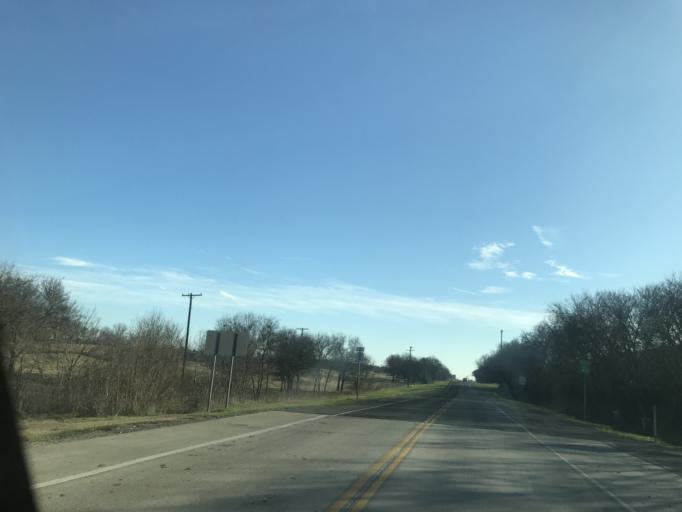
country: US
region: Texas
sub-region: Ellis County
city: Ferris
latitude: 32.5464
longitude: -96.6655
